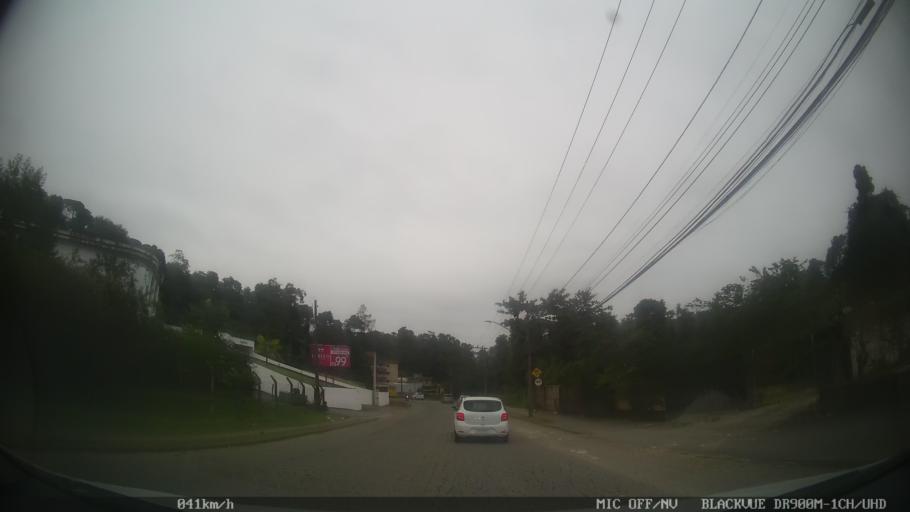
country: BR
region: Santa Catarina
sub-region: Joinville
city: Joinville
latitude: -26.3306
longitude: -48.8573
